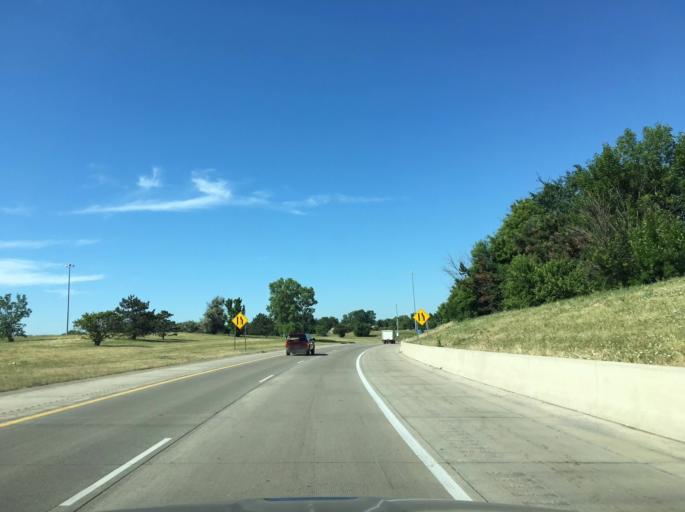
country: US
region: Michigan
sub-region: Macomb County
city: Roseville
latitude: 42.4975
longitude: -82.9193
